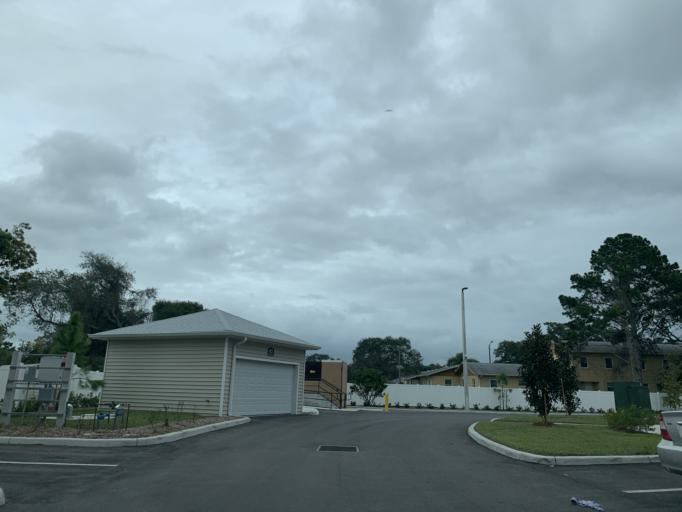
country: US
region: Florida
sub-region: Pinellas County
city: Belleair
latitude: 27.9443
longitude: -82.7945
